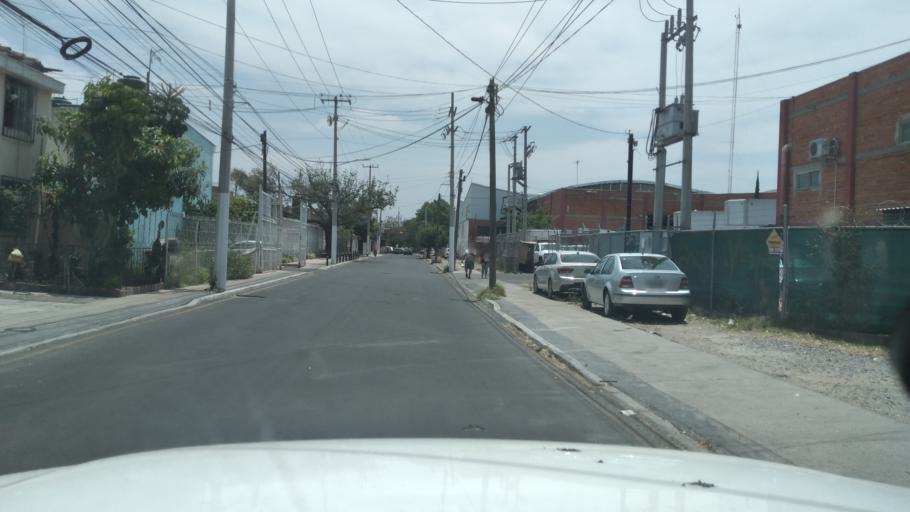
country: MX
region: Jalisco
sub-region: Zapopan
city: Zapopan
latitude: 20.7325
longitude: -103.3715
